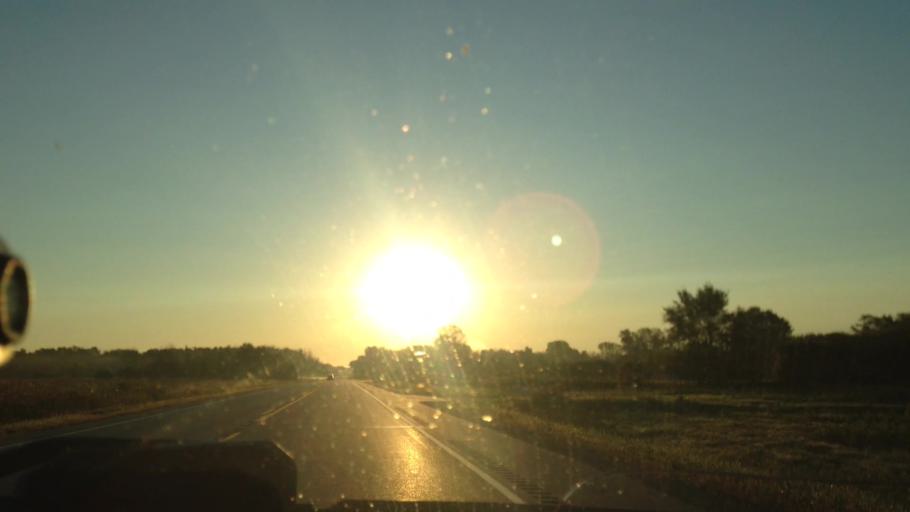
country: US
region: Wisconsin
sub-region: Washington County
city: West Bend
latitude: 43.4263
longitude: -88.1197
